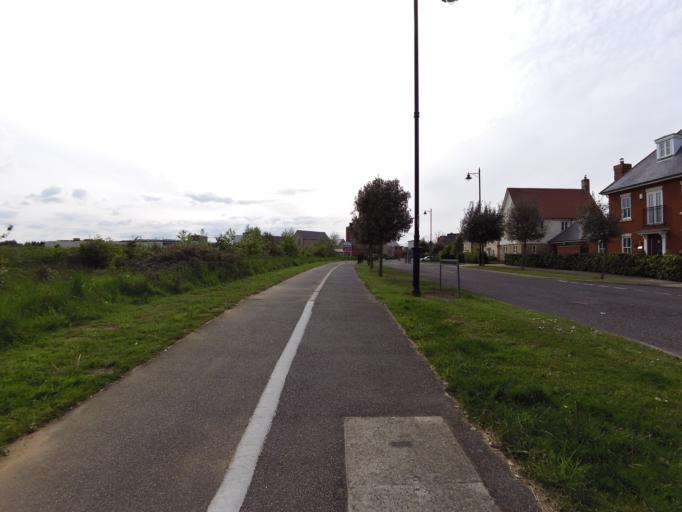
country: GB
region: England
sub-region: Suffolk
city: Ipswich
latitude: 52.0261
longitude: 1.1960
